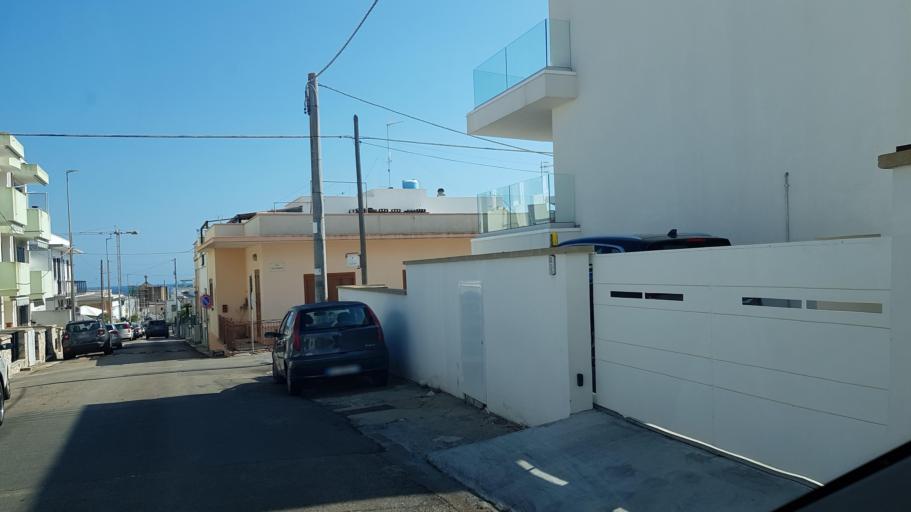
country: IT
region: Apulia
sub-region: Provincia di Lecce
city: Leuca
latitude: 39.8004
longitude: 18.3539
